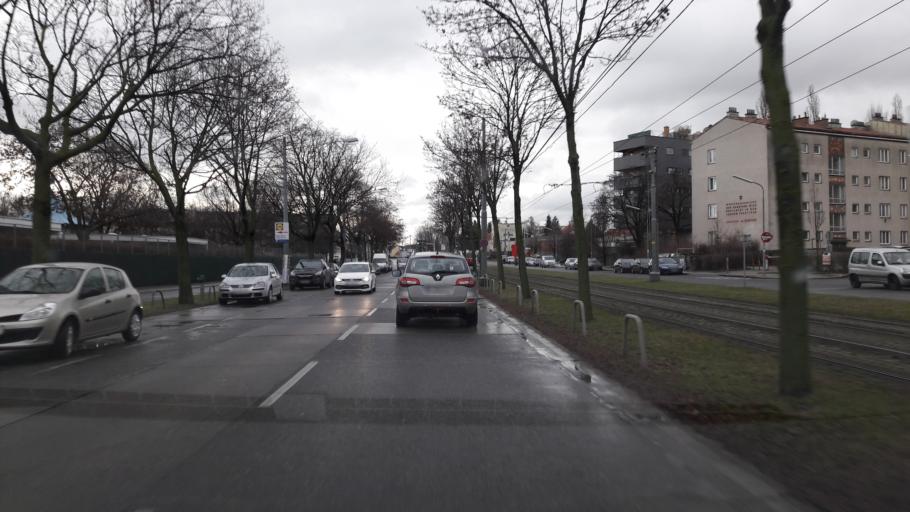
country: AT
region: Lower Austria
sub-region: Politischer Bezirk Wien-Umgebung
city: Schwechat
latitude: 48.1637
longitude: 16.4273
